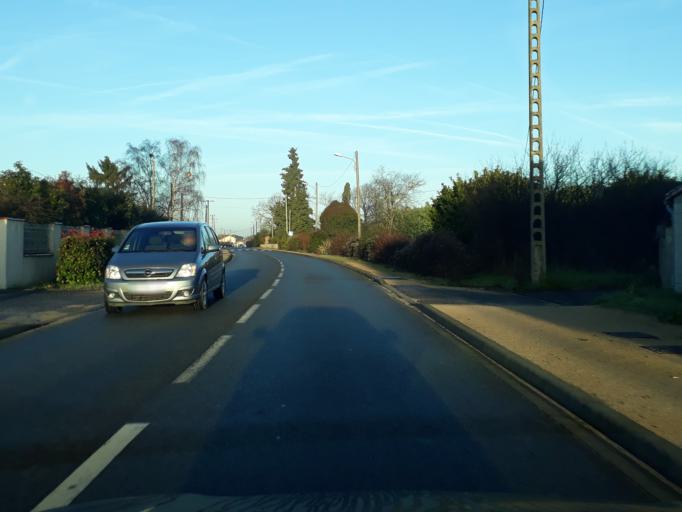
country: FR
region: Midi-Pyrenees
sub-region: Departement de la Haute-Garonne
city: Longages
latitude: 43.3563
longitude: 1.2342
